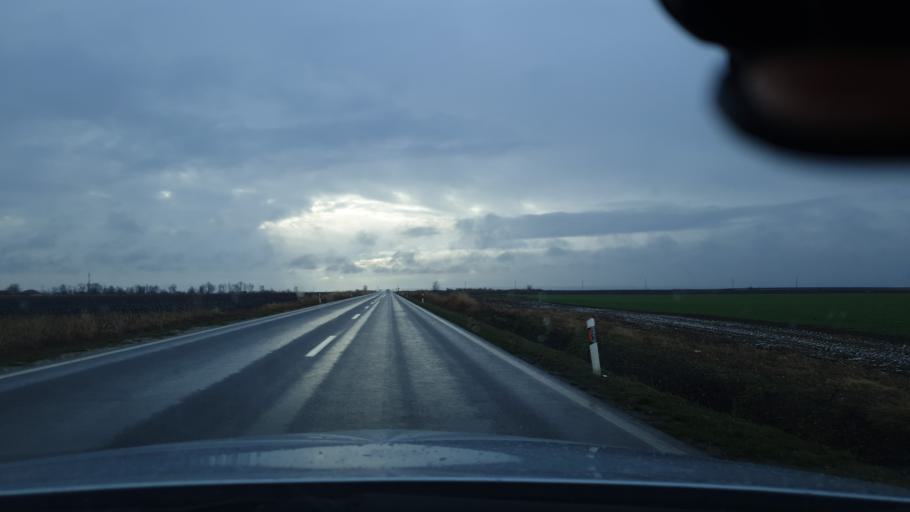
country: RS
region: Autonomna Pokrajina Vojvodina
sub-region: Juznobanatski Okrug
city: Kovin
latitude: 44.8206
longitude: 20.8531
